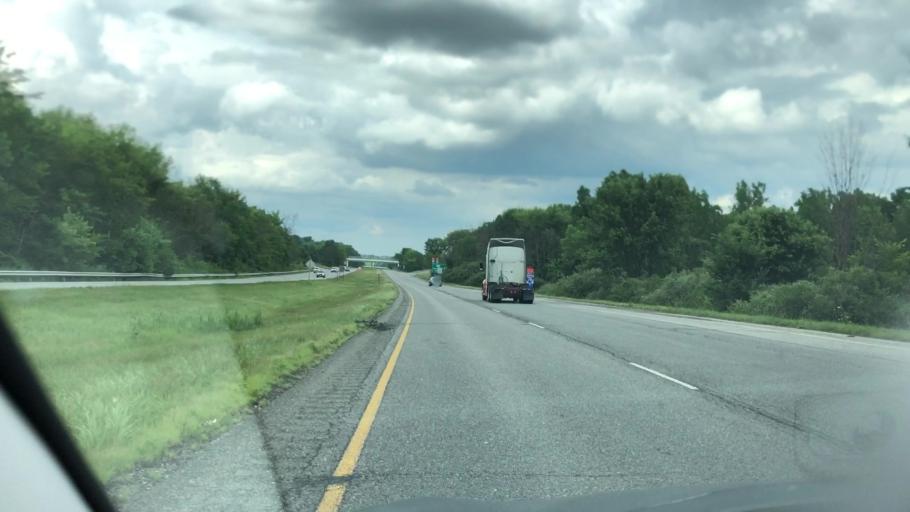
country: US
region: Ohio
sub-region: Summit County
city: Norton
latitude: 41.0437
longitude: -81.6622
